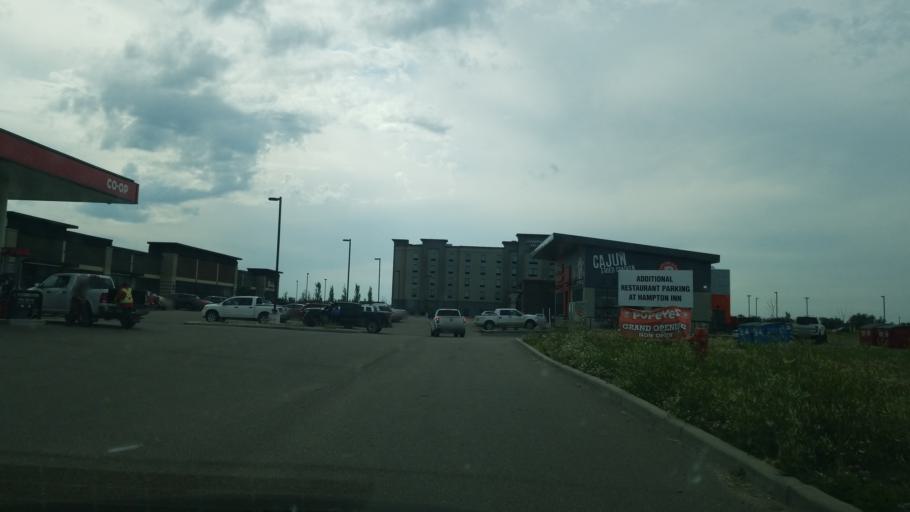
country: CA
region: Saskatchewan
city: Lloydminster
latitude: 53.2791
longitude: -110.0635
